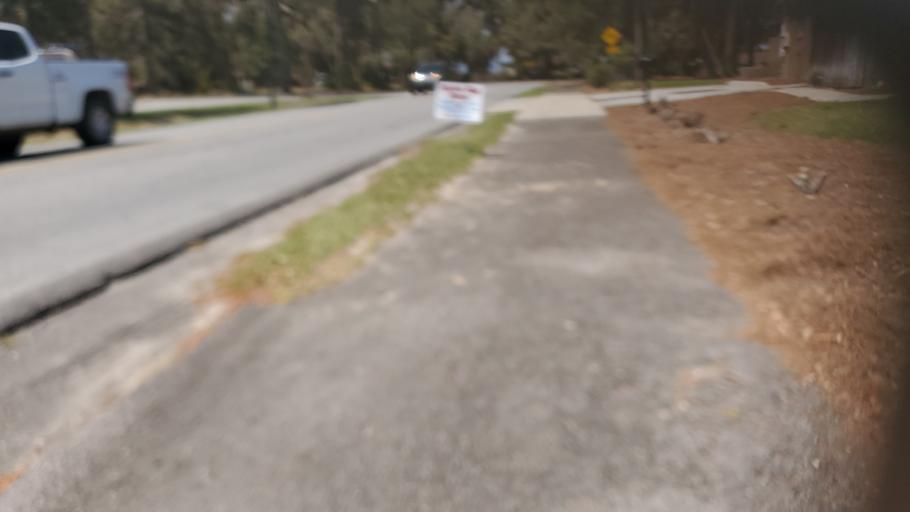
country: US
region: Georgia
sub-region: Chatham County
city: Wilmington Island
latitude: 32.0062
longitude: -80.9881
